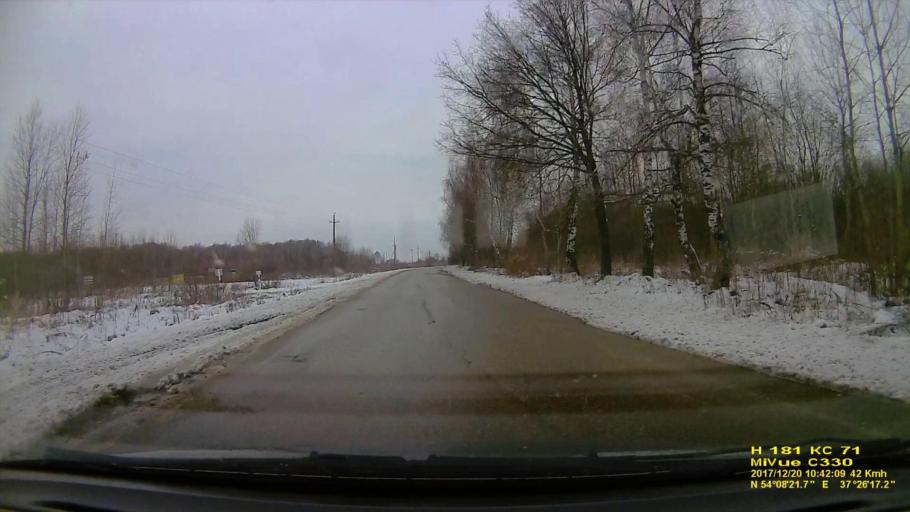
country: RU
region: Tula
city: Kosaya Gora
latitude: 54.1396
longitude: 37.4381
